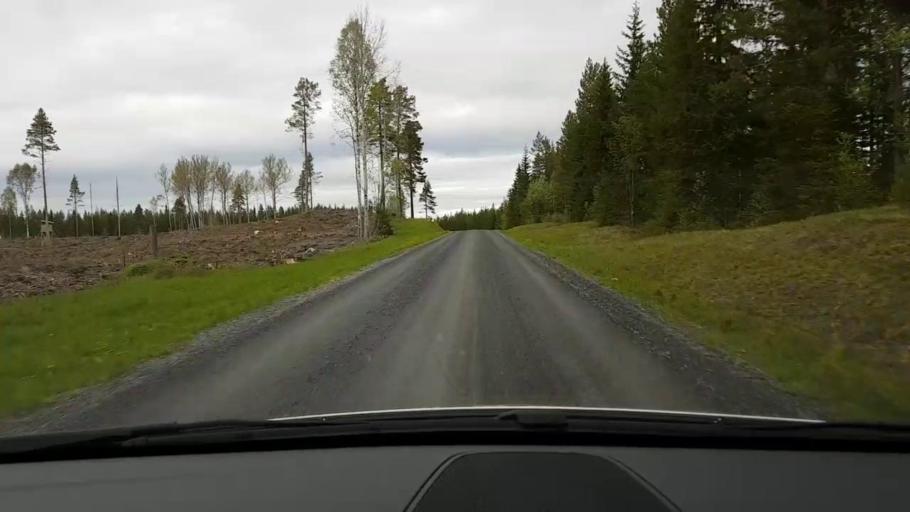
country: SE
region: Jaemtland
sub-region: Krokoms Kommun
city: Krokom
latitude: 63.3002
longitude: 14.3975
